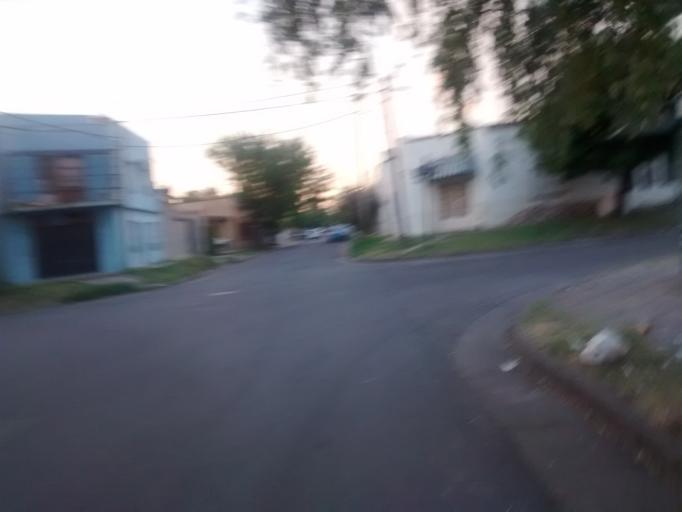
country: AR
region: Buenos Aires
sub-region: Partido de La Plata
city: La Plata
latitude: -34.9406
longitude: -57.9274
